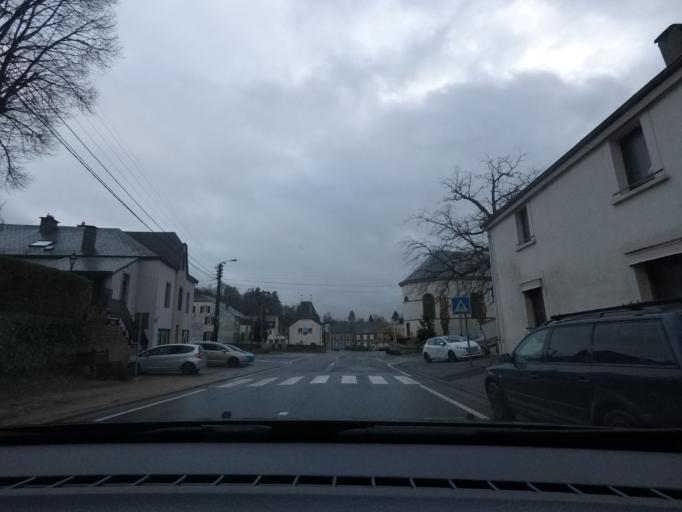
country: BE
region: Wallonia
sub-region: Province du Luxembourg
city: Tintigny
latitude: 49.7182
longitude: 5.4858
